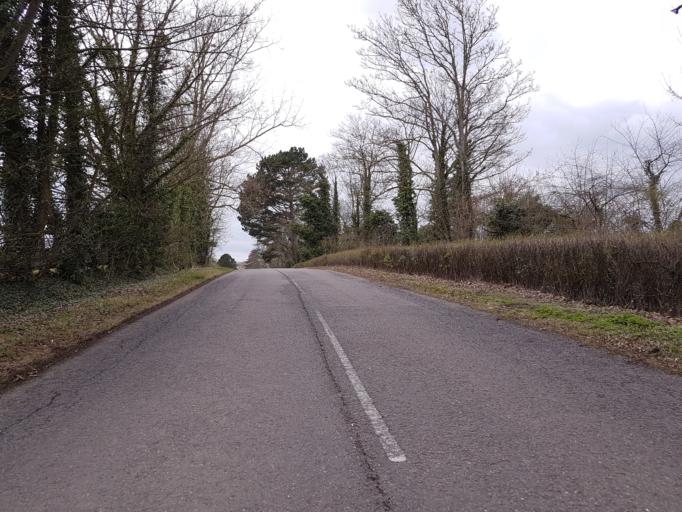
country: GB
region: England
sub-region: Cambridgeshire
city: Girton
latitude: 52.2176
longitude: 0.0593
